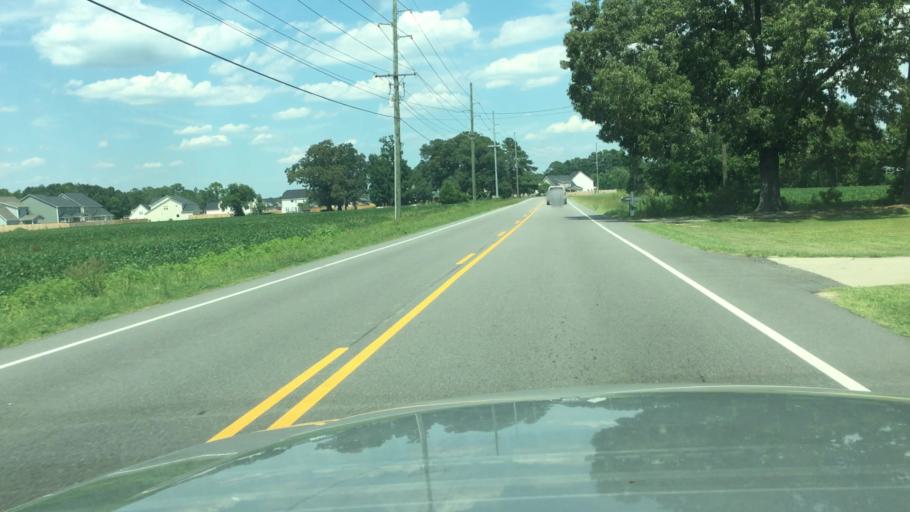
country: US
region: North Carolina
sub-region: Cumberland County
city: Hope Mills
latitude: 34.9487
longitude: -78.8611
